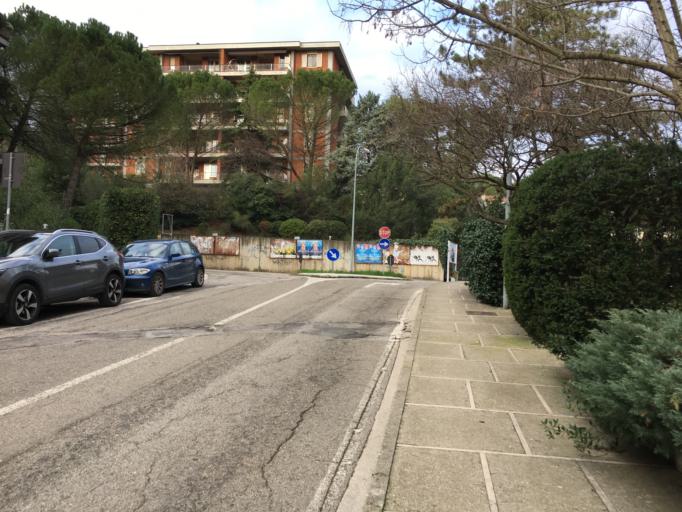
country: IT
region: Umbria
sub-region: Provincia di Perugia
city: Perugia
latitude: 43.1017
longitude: 12.3685
